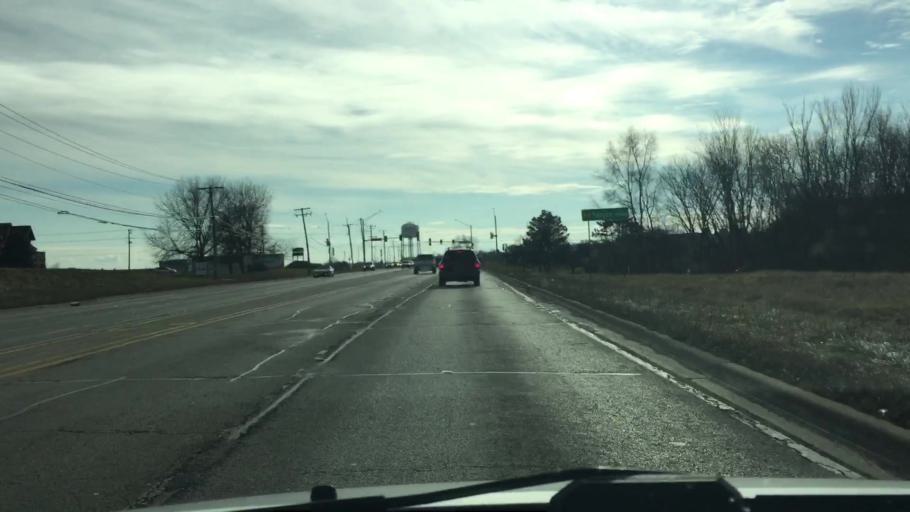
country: US
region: Illinois
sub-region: Kane County
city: Geneva
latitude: 41.8709
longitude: -88.2791
